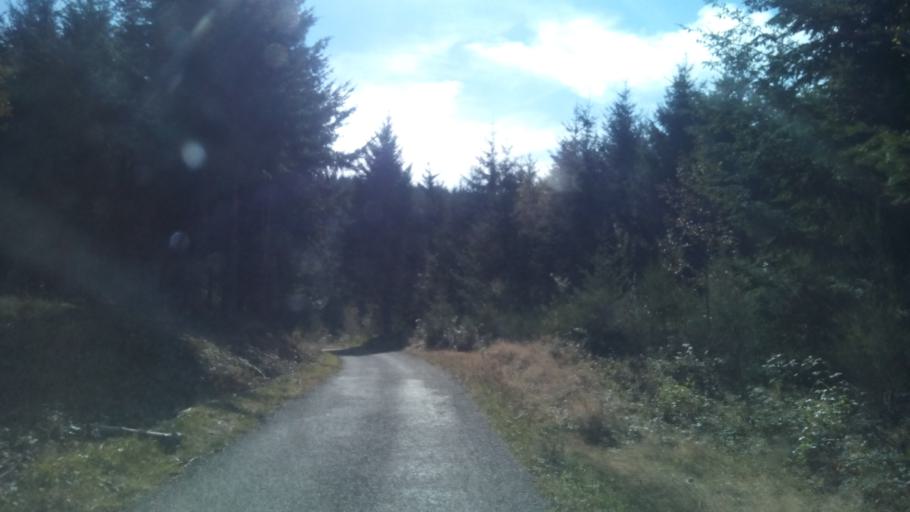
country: FR
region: Bourgogne
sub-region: Departement de Saone-et-Loire
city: Matour
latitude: 46.2020
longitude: 4.4859
